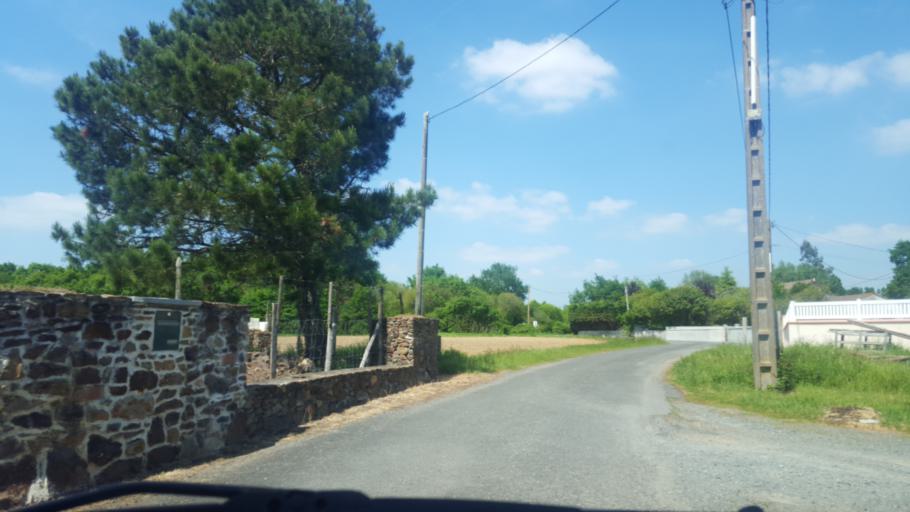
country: FR
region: Pays de la Loire
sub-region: Departement de la Loire-Atlantique
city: La Limouziniere
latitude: 47.0354
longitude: -1.5850
